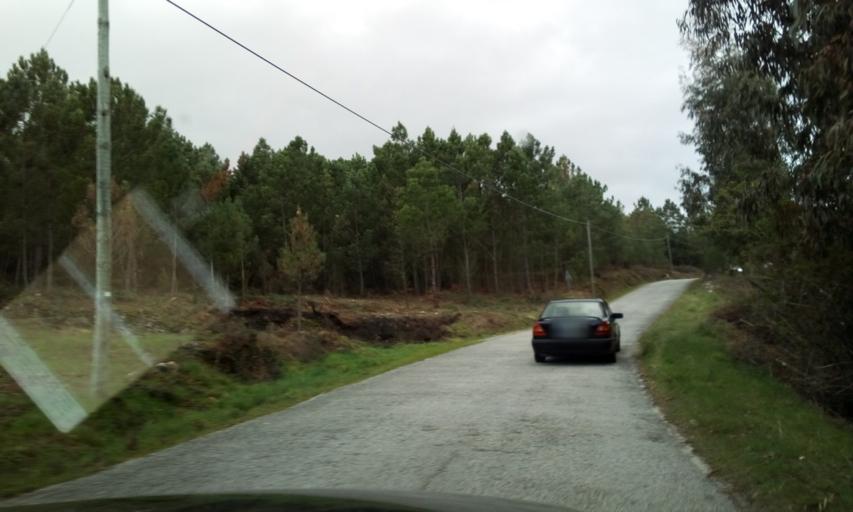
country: PT
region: Guarda
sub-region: Fornos de Algodres
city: Fornos de Algodres
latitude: 40.6365
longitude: -7.5769
